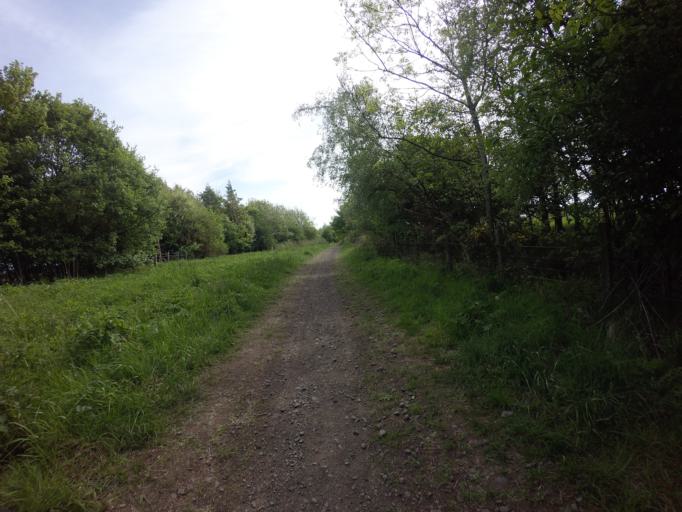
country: GB
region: Scotland
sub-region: West Lothian
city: Mid Calder
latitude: 55.9152
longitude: -3.4932
